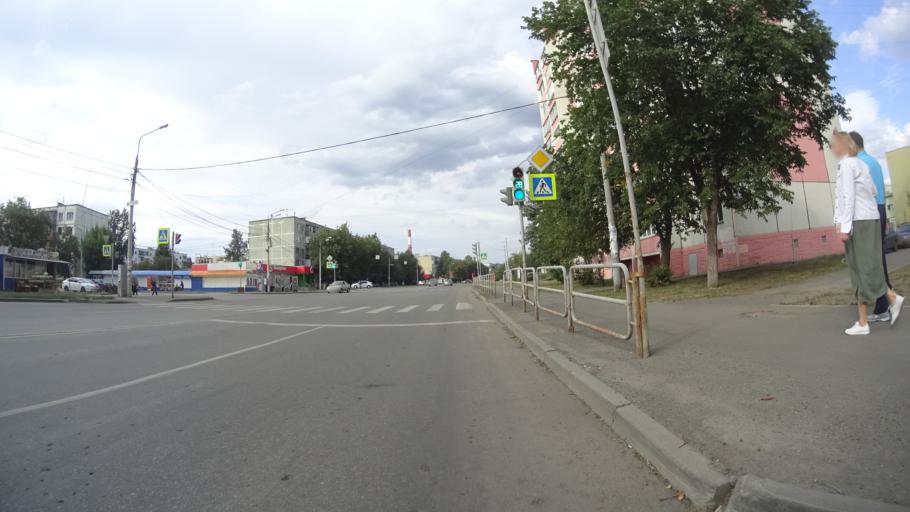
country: RU
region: Chelyabinsk
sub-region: Gorod Chelyabinsk
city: Chelyabinsk
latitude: 55.1984
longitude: 61.3183
